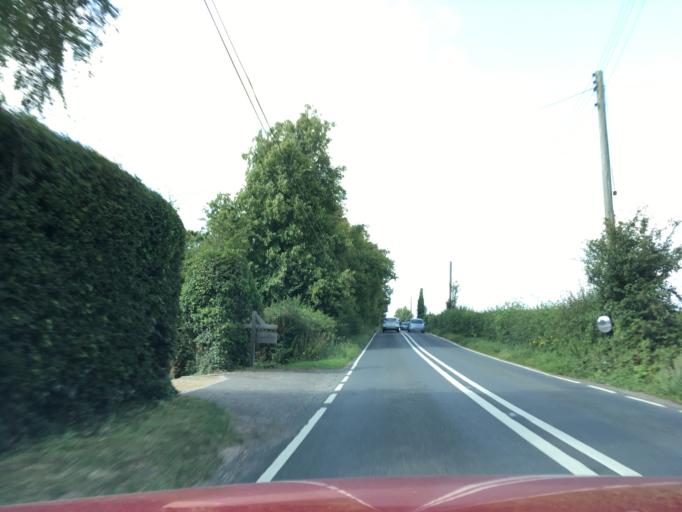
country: GB
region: England
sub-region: Kent
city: Headcorn
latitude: 51.1451
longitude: 0.6401
